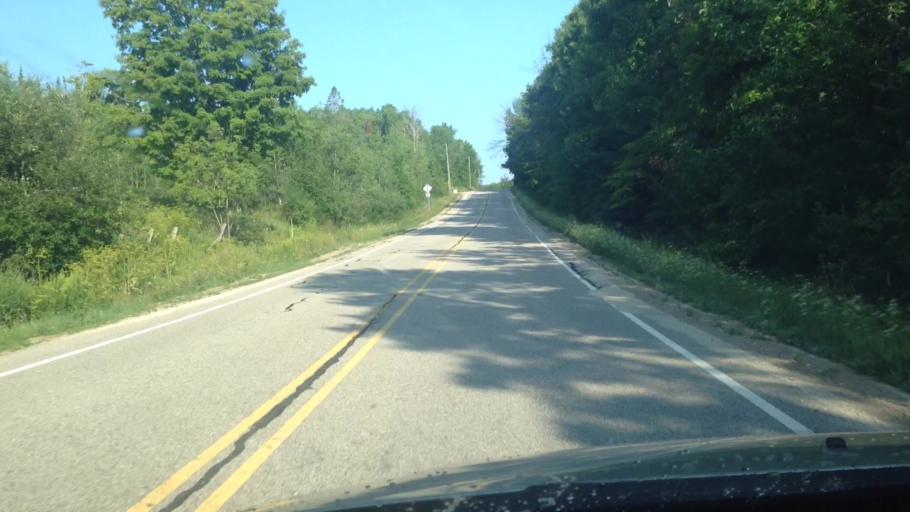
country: US
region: Michigan
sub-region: Mackinac County
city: Saint Ignace
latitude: 45.8915
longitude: -84.7918
